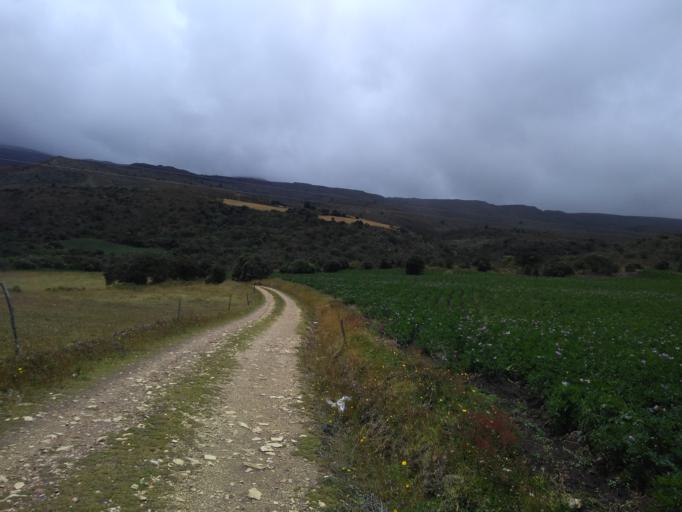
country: CO
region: Boyaca
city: Toca
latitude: 5.5870
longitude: -73.1245
